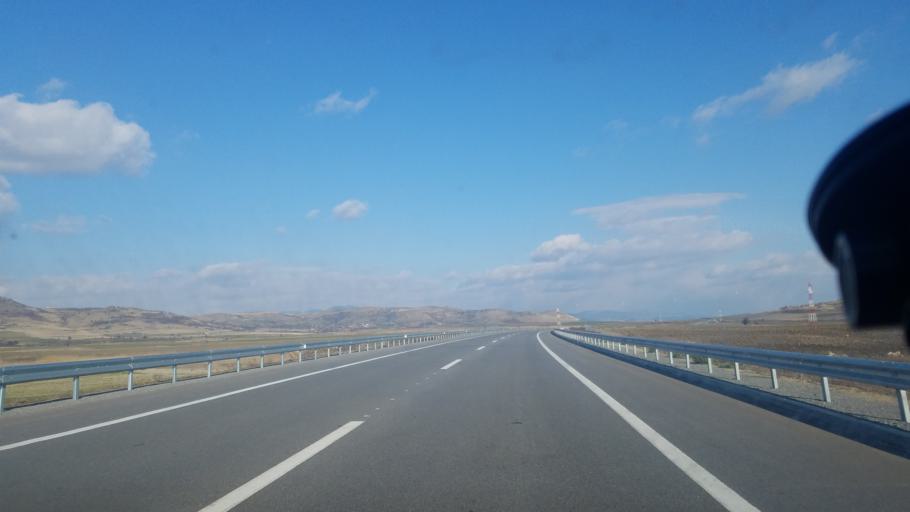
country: MK
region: Karbinci
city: Karbinci
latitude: 41.8134
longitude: 22.1716
